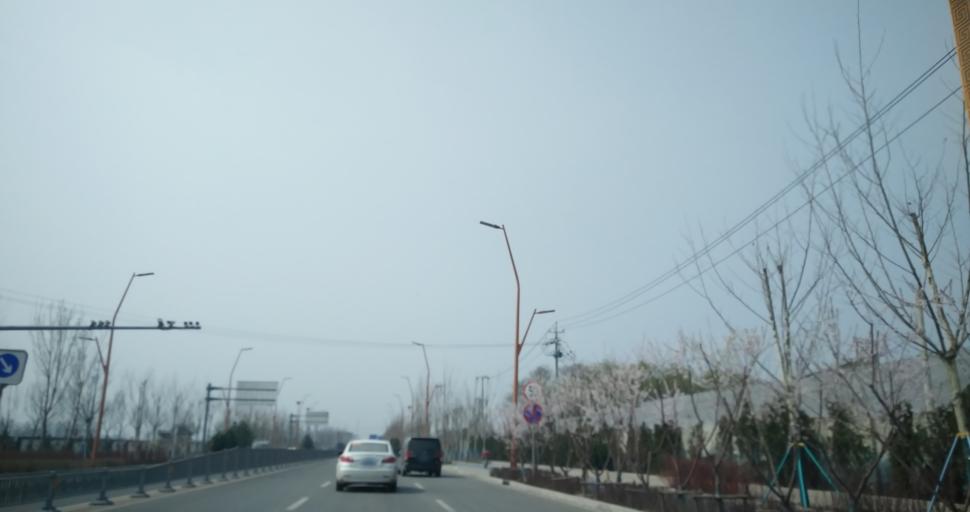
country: CN
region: Beijing
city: Weishanzhuang
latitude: 39.6843
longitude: 116.4136
